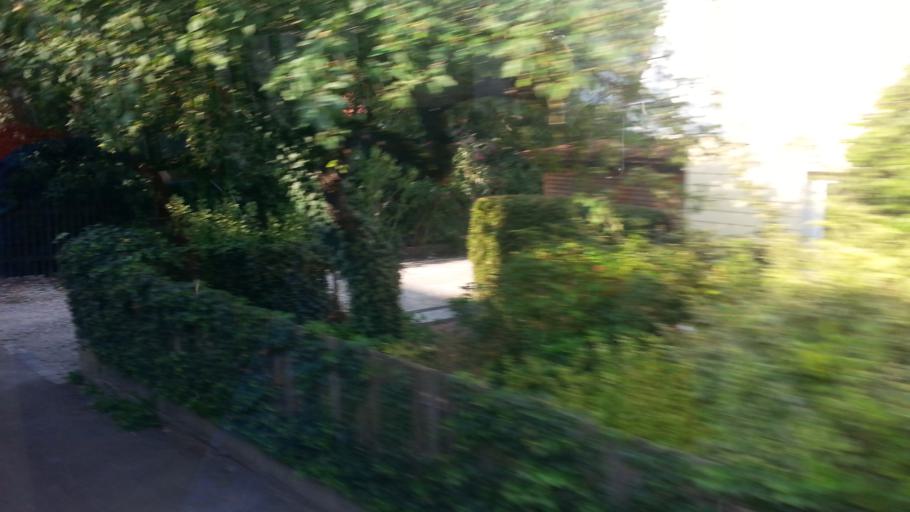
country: DE
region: Bavaria
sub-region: Upper Bavaria
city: Neufahrn bei Freising
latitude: 48.2803
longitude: 11.6743
